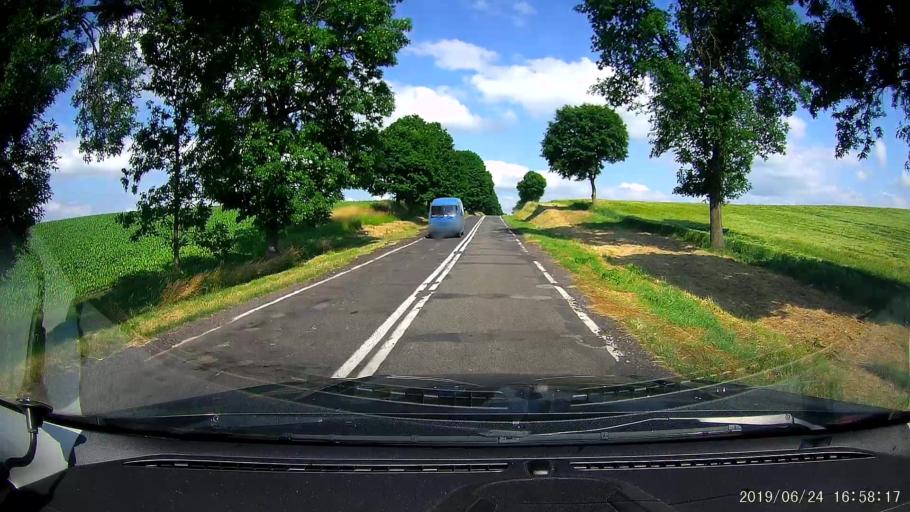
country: PL
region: Lublin Voivodeship
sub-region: Powiat tomaszowski
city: Telatyn
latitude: 50.5254
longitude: 23.8772
